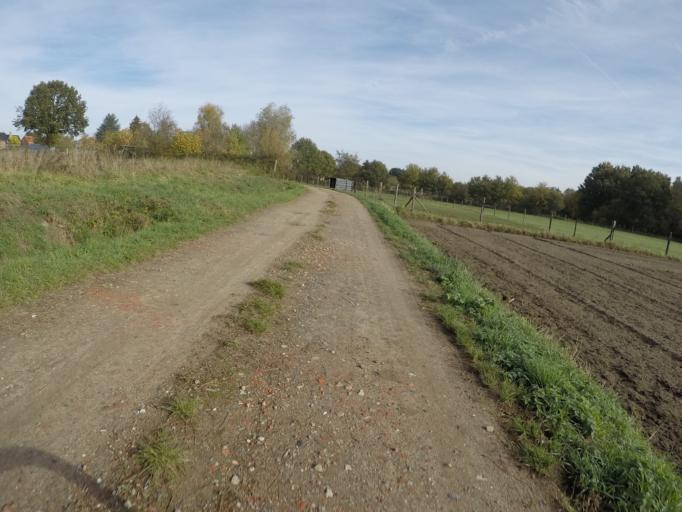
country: BE
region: Flanders
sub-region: Provincie Vlaams-Brabant
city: Begijnendijk
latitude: 50.9862
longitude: 4.7904
